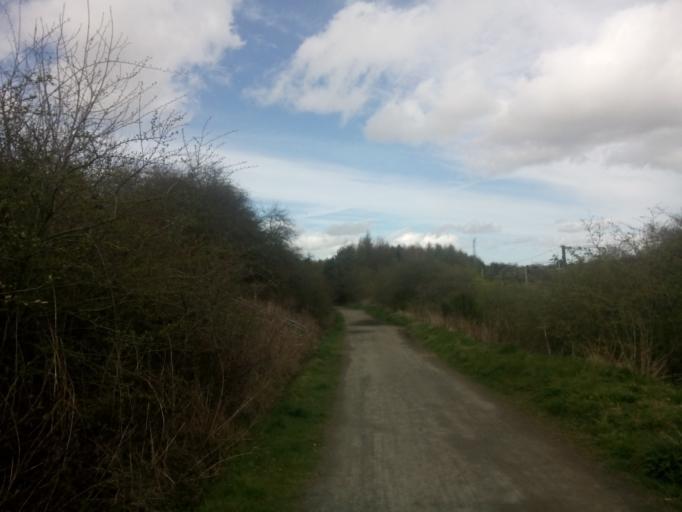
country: GB
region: England
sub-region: County Durham
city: Durham
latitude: 54.7693
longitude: -1.6067
